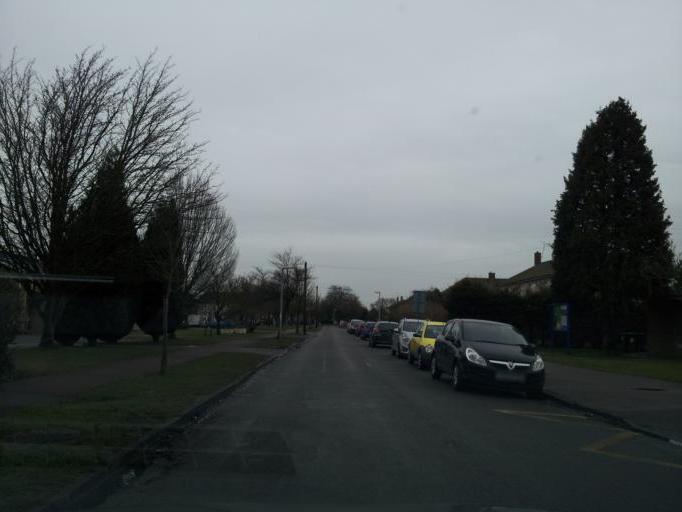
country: GB
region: England
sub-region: Cambridgeshire
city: Cambridge
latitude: 52.1812
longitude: 0.1524
